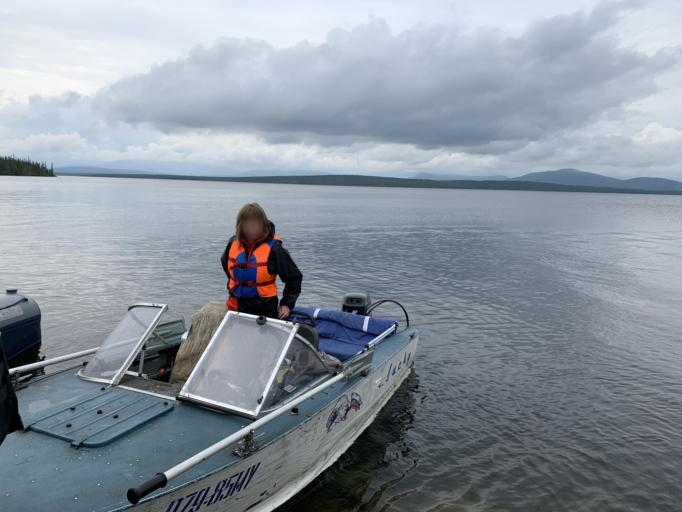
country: RU
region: Murmansk
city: Monchegorsk
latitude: 67.7958
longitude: 33.0524
